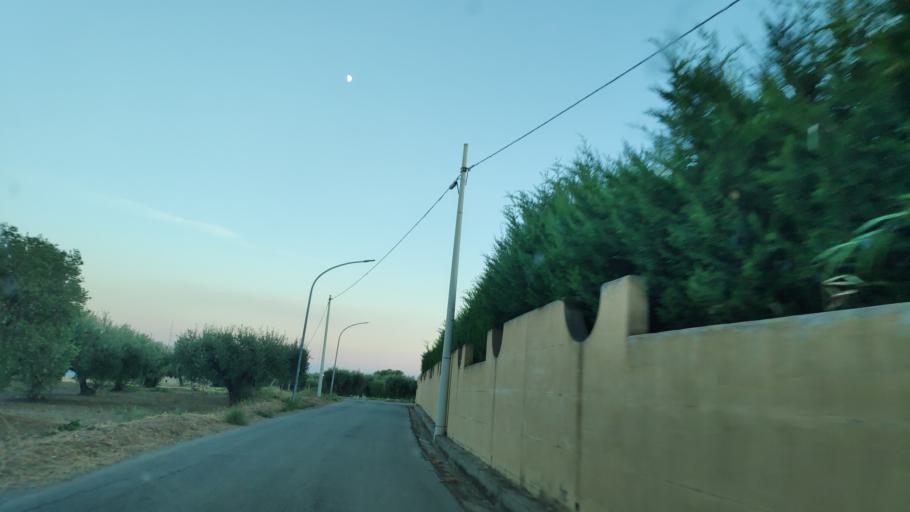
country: IT
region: Calabria
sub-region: Provincia di Reggio Calabria
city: Riace Marina
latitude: 38.3970
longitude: 16.5232
